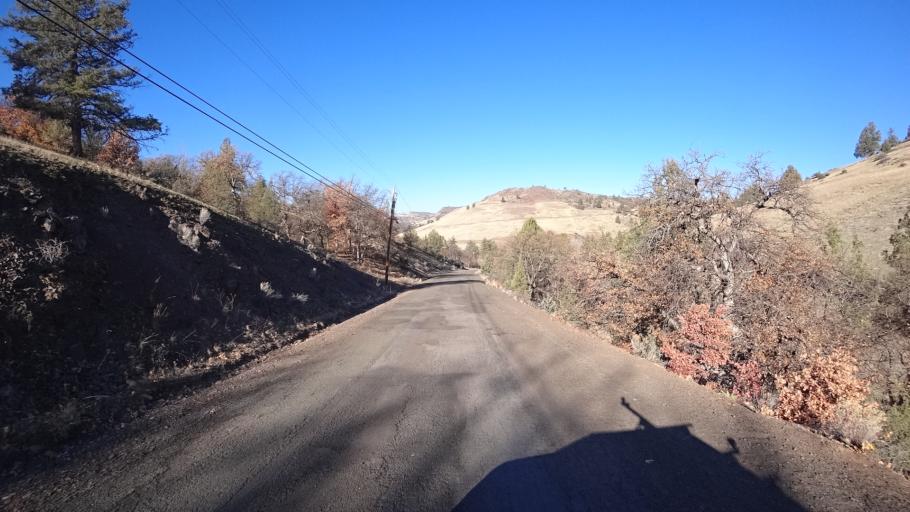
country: US
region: California
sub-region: Siskiyou County
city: Montague
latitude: 41.9156
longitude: -122.4455
